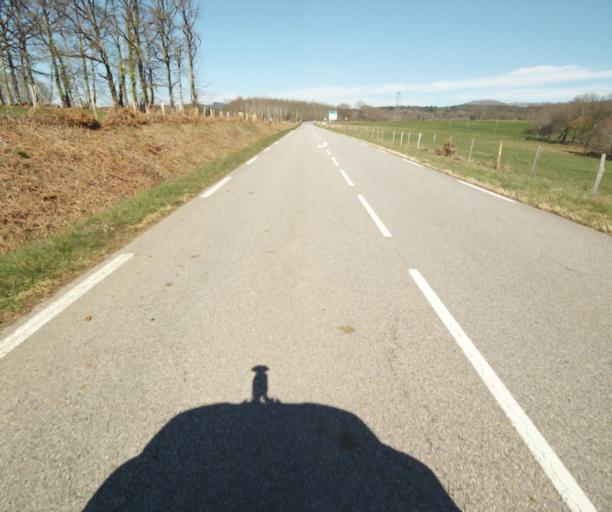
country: FR
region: Limousin
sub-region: Departement de la Correze
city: Chamboulive
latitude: 45.4717
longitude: 1.7580
